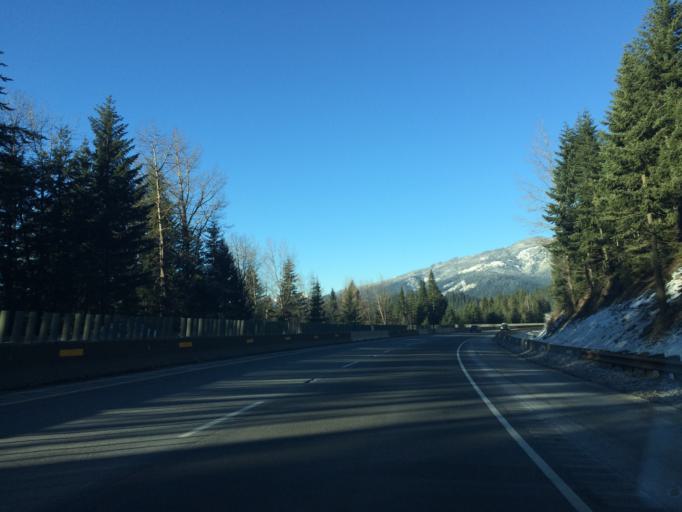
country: US
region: Washington
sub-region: Kittitas County
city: Cle Elum
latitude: 47.2790
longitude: -121.2803
